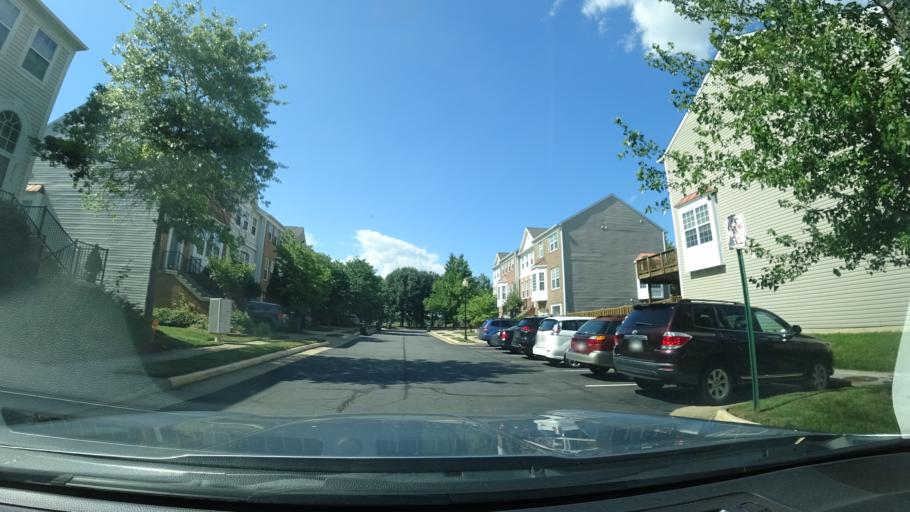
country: US
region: Virginia
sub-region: Loudoun County
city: Broadlands
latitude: 38.9935
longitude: -77.4878
